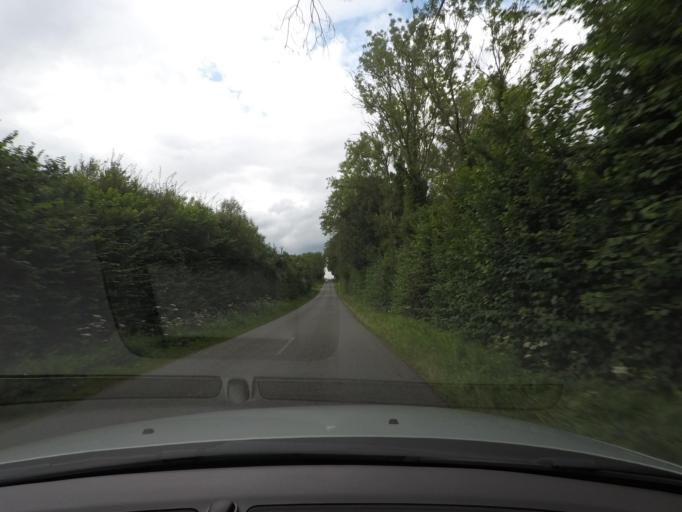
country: FR
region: Haute-Normandie
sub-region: Departement de l'Eure
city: Les Andelys
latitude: 49.2699
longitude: 1.3594
